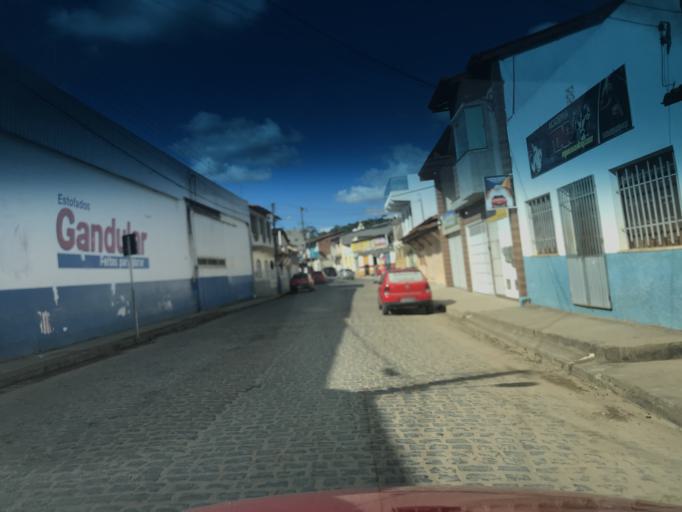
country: BR
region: Bahia
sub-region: Gandu
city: Gandu
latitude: -13.7471
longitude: -39.4904
